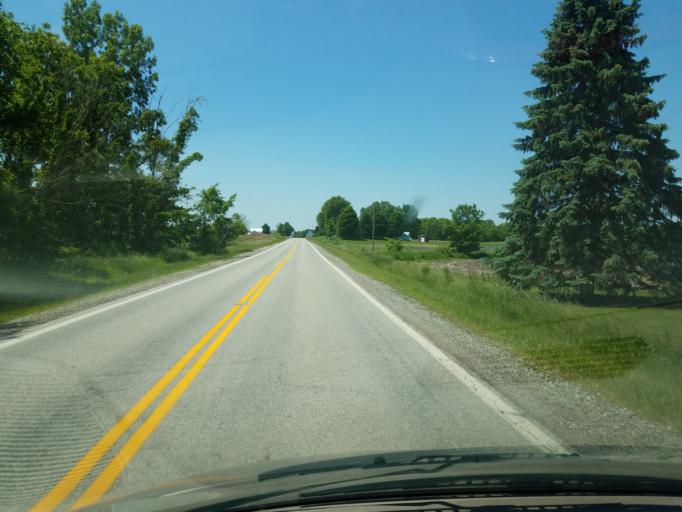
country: US
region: Ohio
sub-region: Knox County
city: Centerburg
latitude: 40.3754
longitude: -82.7341
